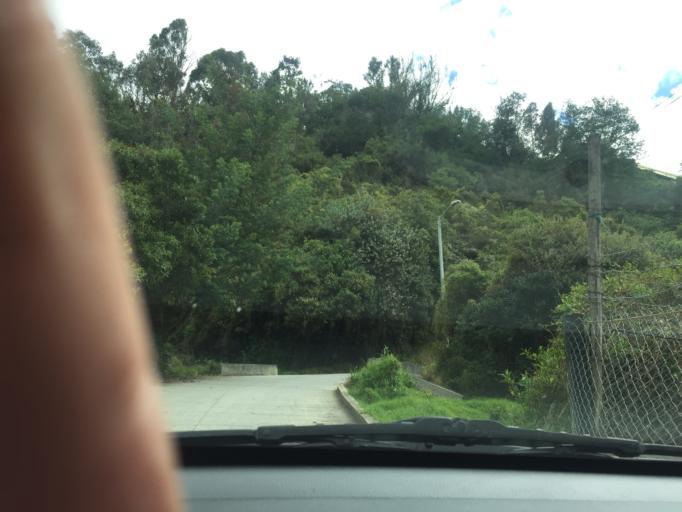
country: CO
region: Cundinamarca
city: Tocancipa
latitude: 4.9642
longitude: -73.8966
